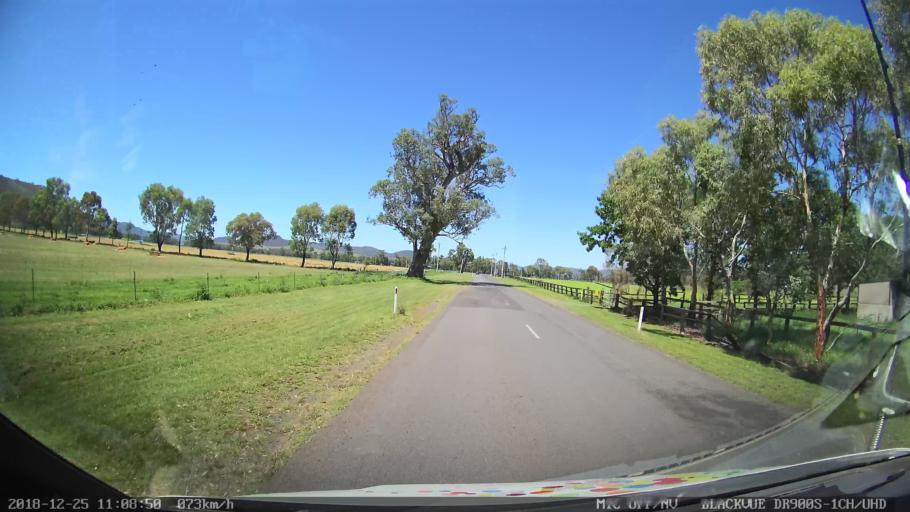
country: AU
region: New South Wales
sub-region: Upper Hunter Shire
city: Merriwa
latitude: -32.4054
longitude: 150.1217
